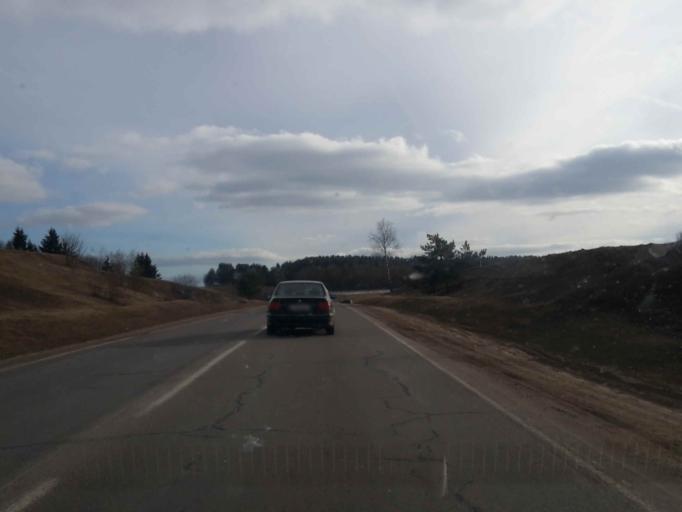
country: BY
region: Minsk
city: Bal'shavik
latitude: 54.0344
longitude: 27.5605
